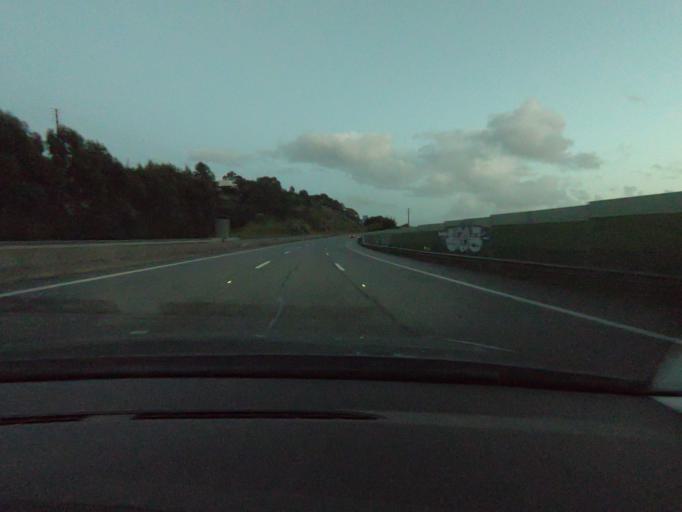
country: PT
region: Lisbon
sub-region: Oeiras
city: Barcarena
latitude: 38.7327
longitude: -9.2751
